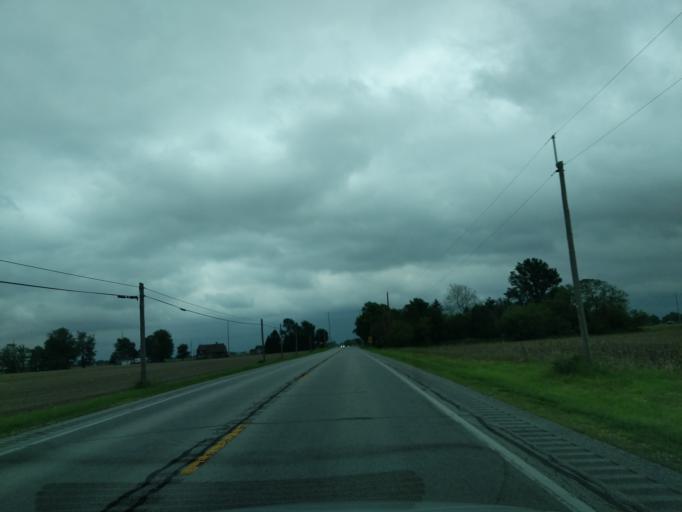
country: US
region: Indiana
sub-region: Madison County
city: Frankton
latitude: 40.2775
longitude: -85.7707
